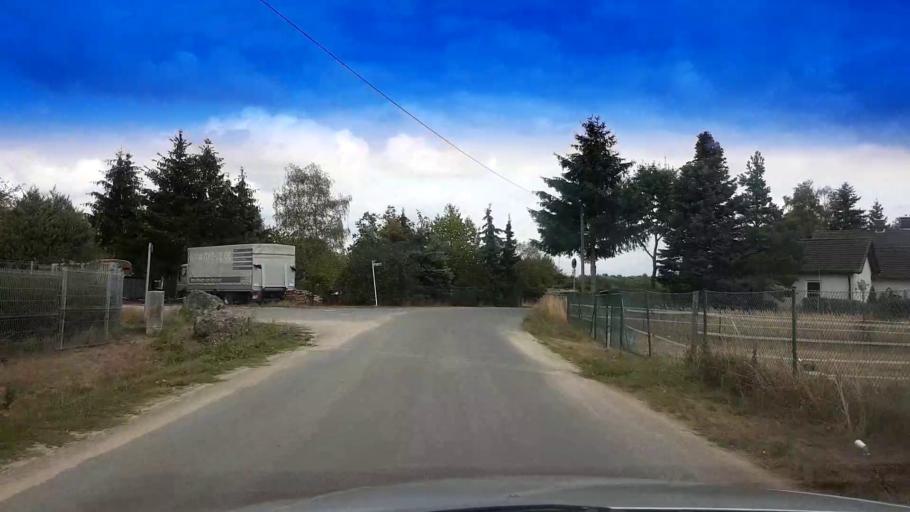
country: DE
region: Bavaria
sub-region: Upper Franconia
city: Bamberg
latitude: 49.8779
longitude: 10.9225
